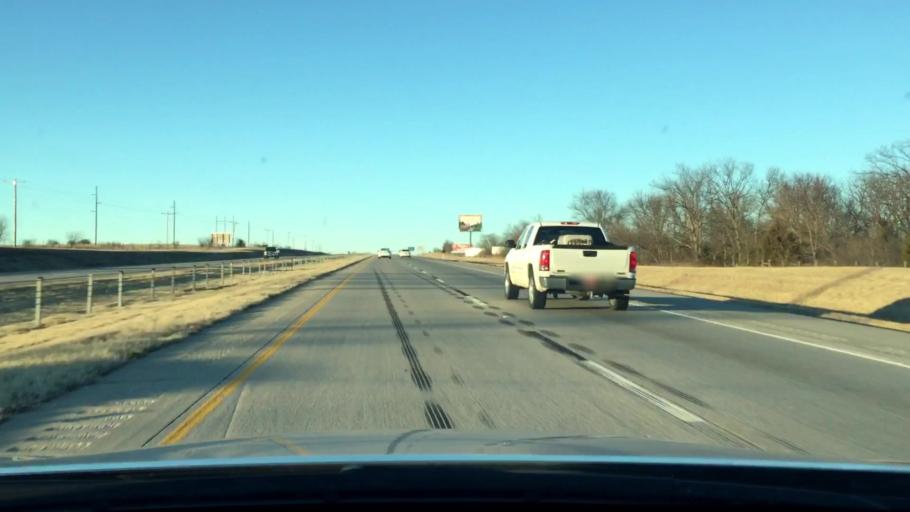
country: US
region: Oklahoma
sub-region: Love County
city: Marietta
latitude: 33.8850
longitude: -97.1343
